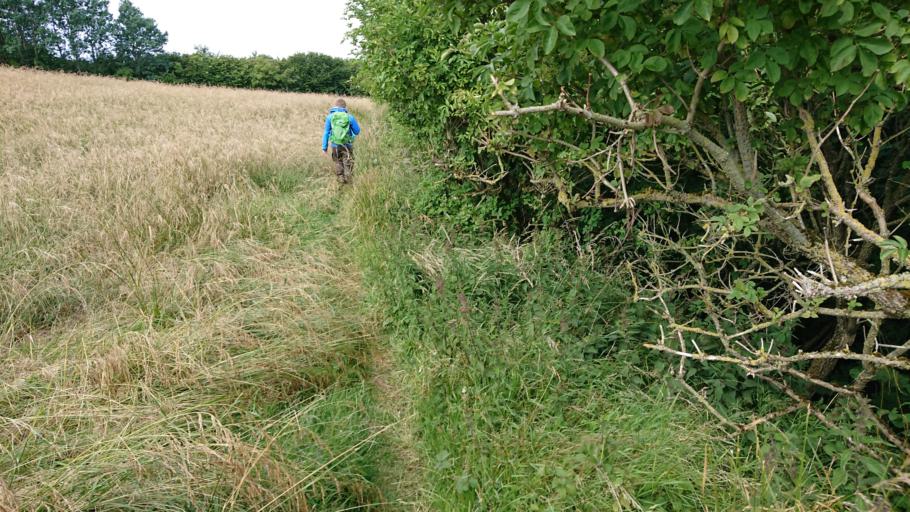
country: DK
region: North Denmark
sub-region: Jammerbugt Kommune
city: Brovst
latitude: 57.1322
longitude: 9.4039
